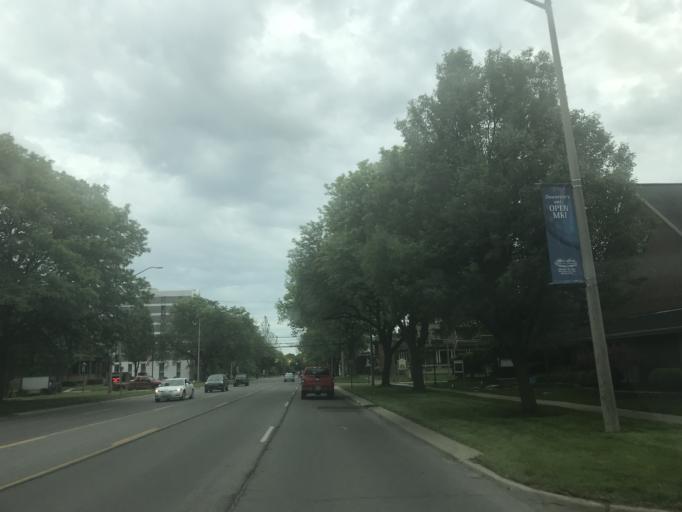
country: US
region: Michigan
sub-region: Wayne County
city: Wyandotte
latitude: 42.2084
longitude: -83.1484
